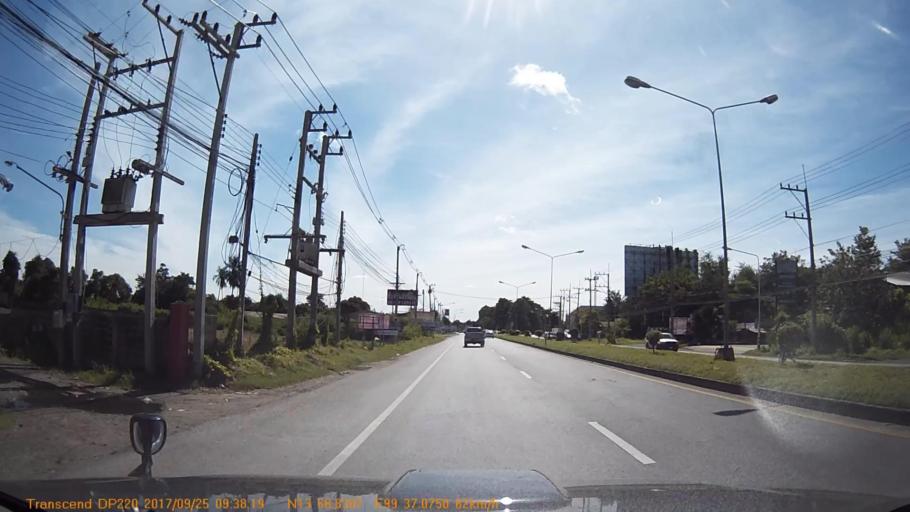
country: TH
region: Kanchanaburi
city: Tha Muang
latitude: 13.9806
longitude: 99.6180
